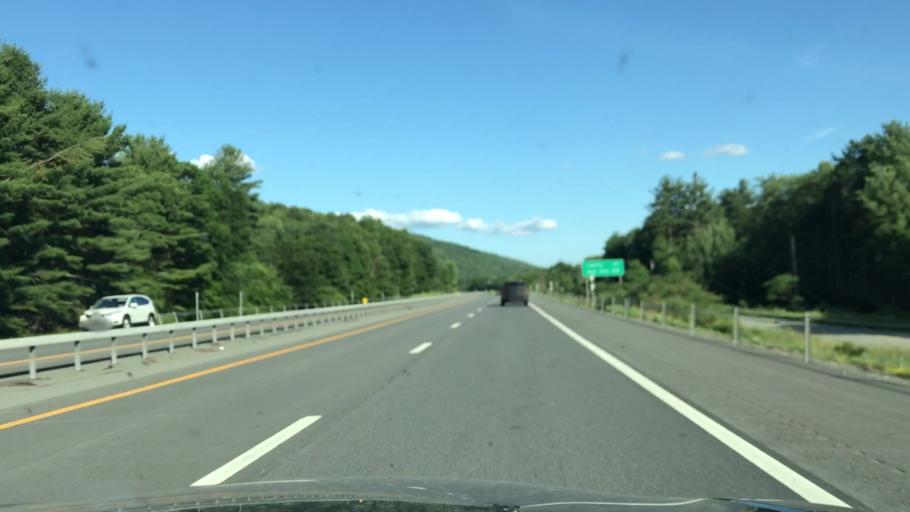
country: US
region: New York
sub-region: Delaware County
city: Hancock
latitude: 41.9852
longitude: -75.1143
